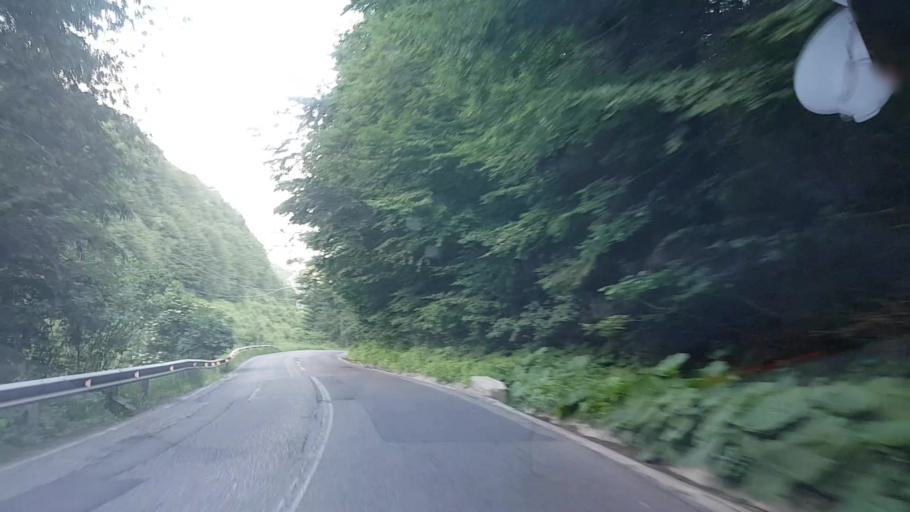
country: RO
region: Harghita
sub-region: Comuna Praid
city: Ocna de Sus
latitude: 46.5998
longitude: 25.2389
